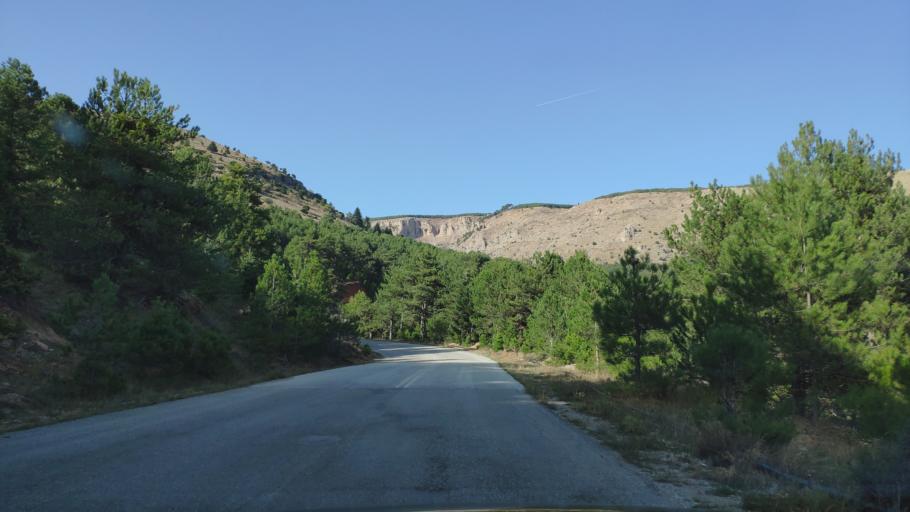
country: GR
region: West Greece
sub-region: Nomos Achaias
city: Aiyira
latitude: 38.0249
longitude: 22.4022
